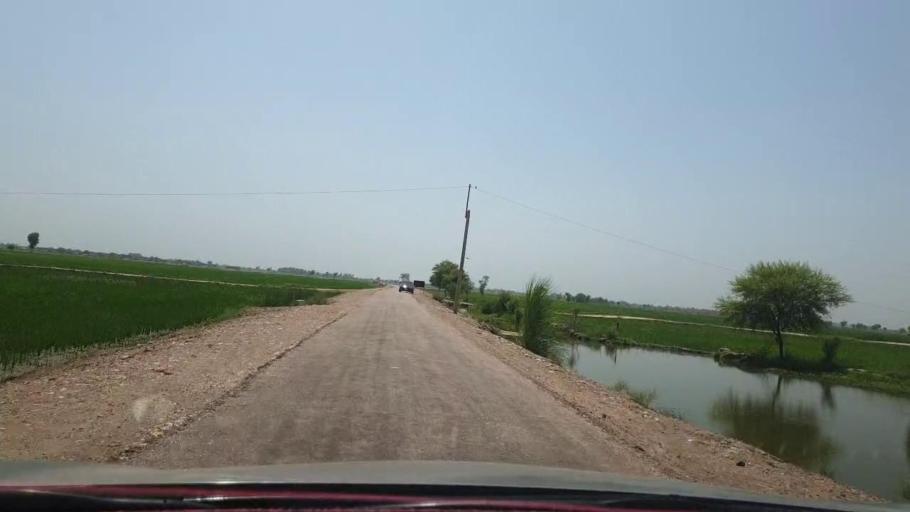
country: PK
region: Sindh
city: Warah
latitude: 27.5556
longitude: 67.7979
